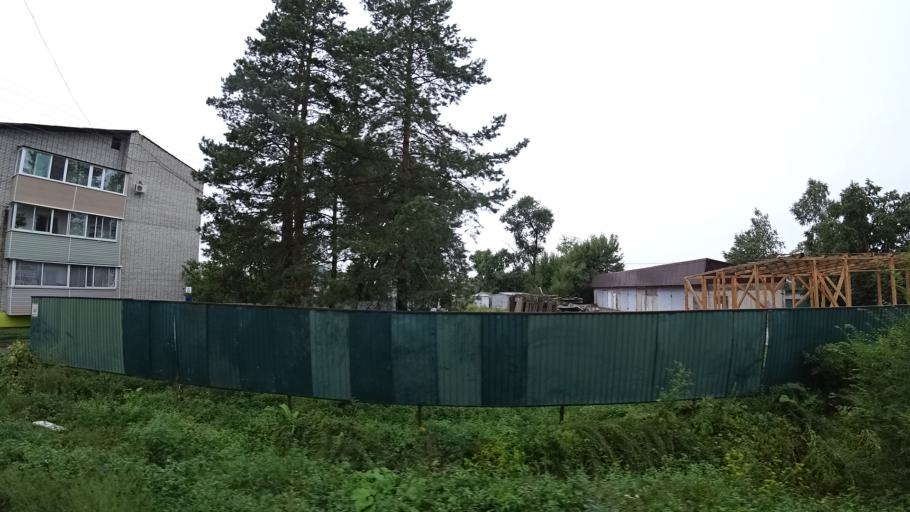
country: RU
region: Primorskiy
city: Monastyrishche
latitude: 44.1945
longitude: 132.4237
